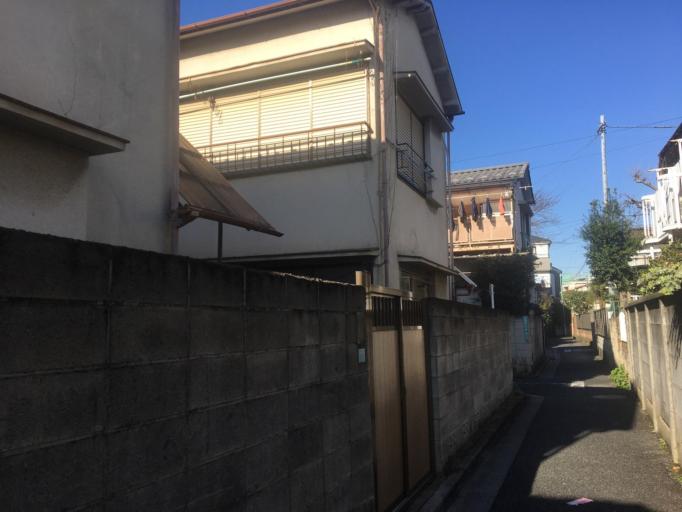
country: JP
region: Tokyo
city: Tokyo
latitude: 35.7377
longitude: 139.6985
